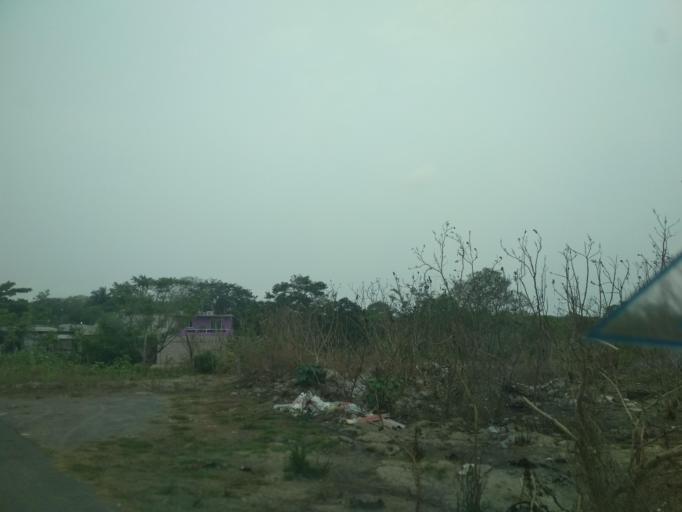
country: MX
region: Veracruz
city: Paso del Toro
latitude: 19.0492
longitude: -96.1515
